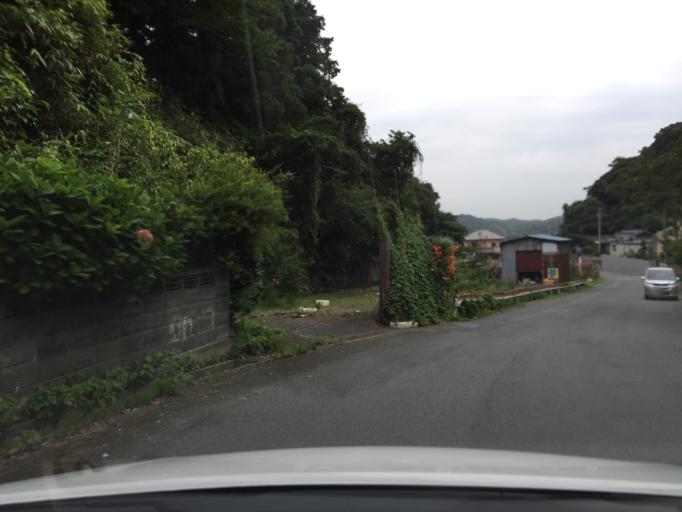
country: JP
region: Fukushima
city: Iwaki
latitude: 37.0091
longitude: 140.9729
